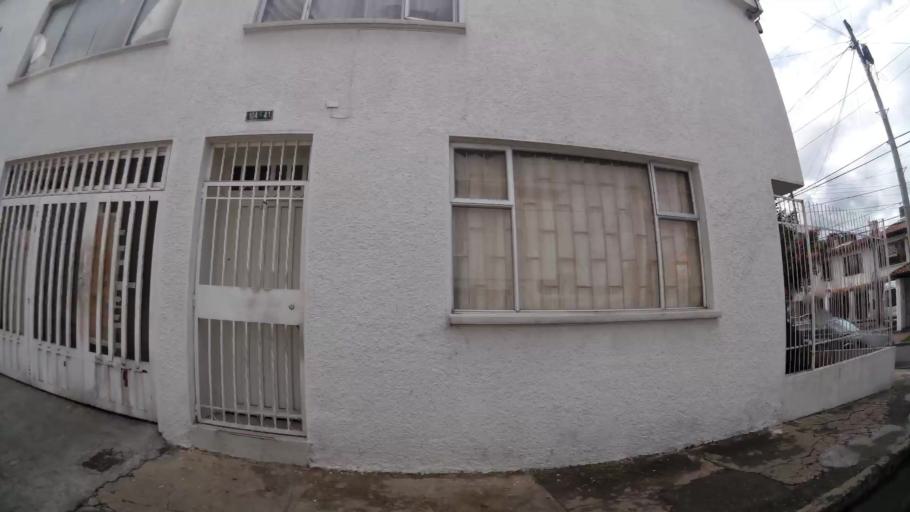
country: CO
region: Bogota D.C.
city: Barrio San Luis
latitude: 4.6934
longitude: -74.0578
